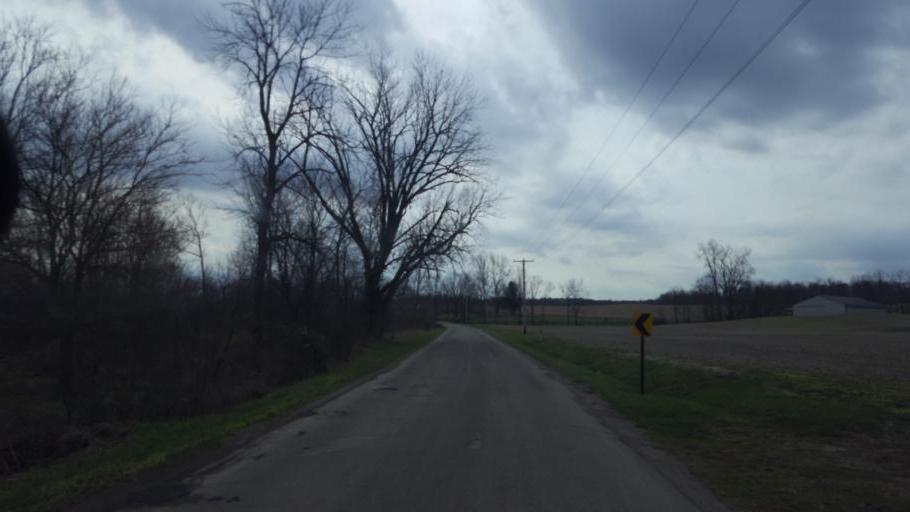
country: US
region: Ohio
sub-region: Morrow County
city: Mount Gilead
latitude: 40.5605
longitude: -82.6927
